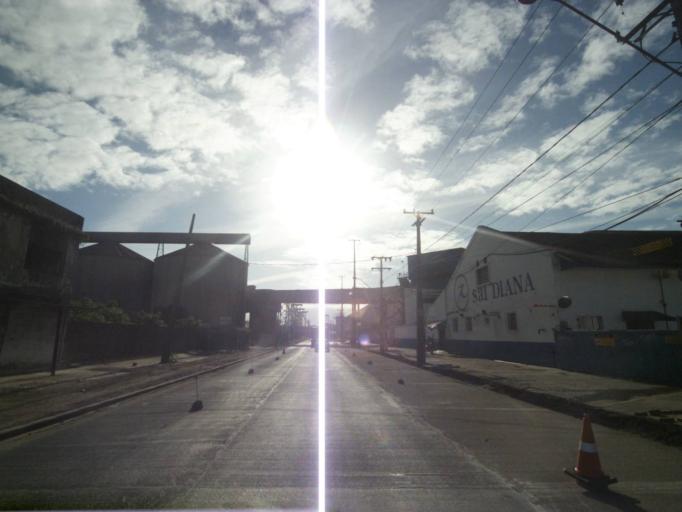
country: BR
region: Parana
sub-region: Paranagua
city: Paranagua
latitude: -25.5060
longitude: -48.5257
